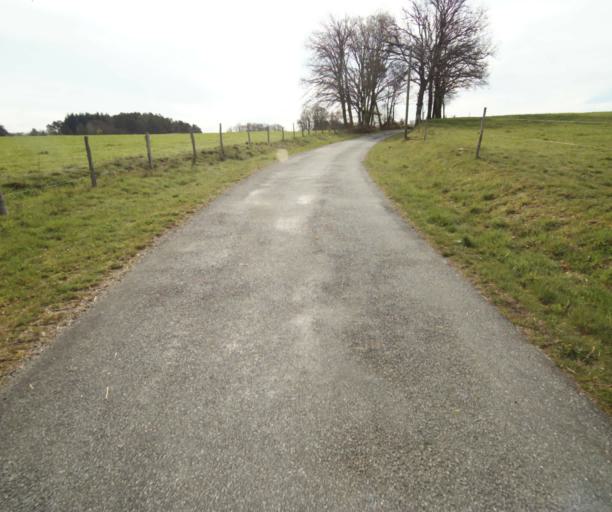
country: FR
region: Limousin
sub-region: Departement de la Correze
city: Correze
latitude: 45.3370
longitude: 1.8668
